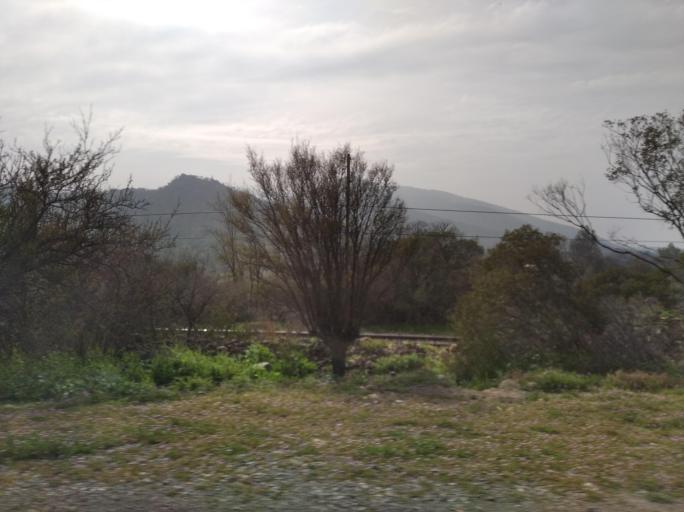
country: CL
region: Santiago Metropolitan
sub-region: Provincia de Chacabuco
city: Lampa
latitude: -33.1453
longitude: -70.9134
